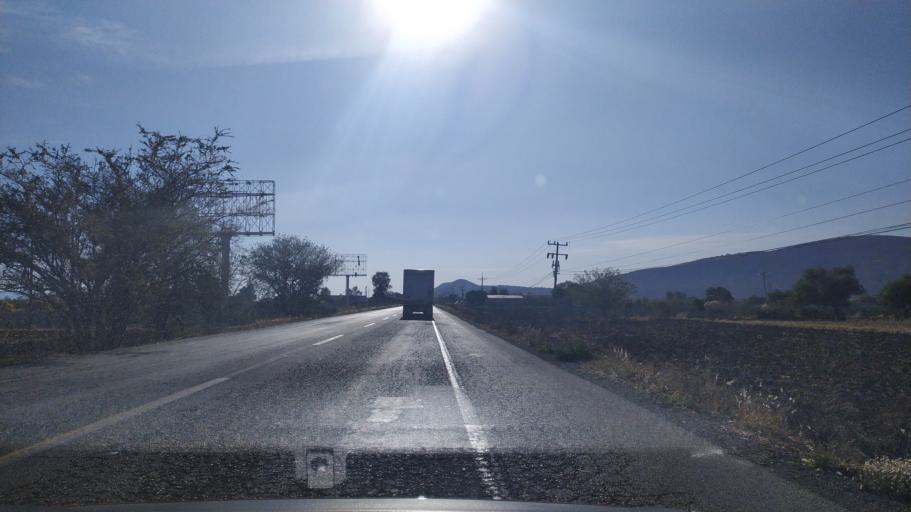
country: MX
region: Jalisco
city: Jamay
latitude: 20.2938
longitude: -102.6549
